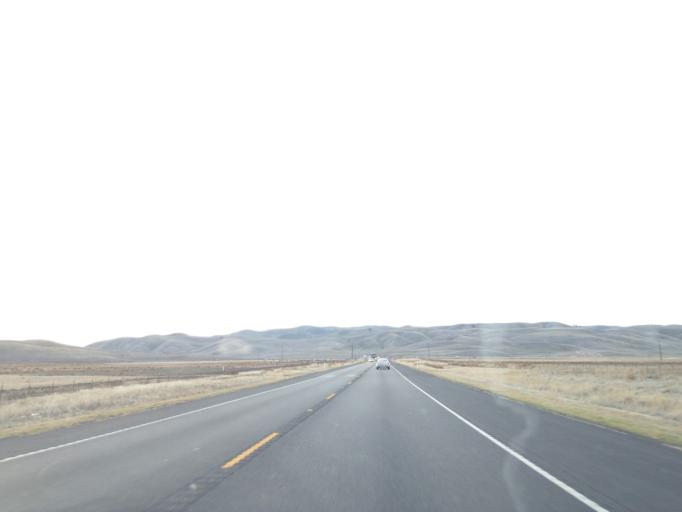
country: US
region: California
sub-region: San Luis Obispo County
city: Shandon
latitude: 35.7360
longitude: -120.2757
